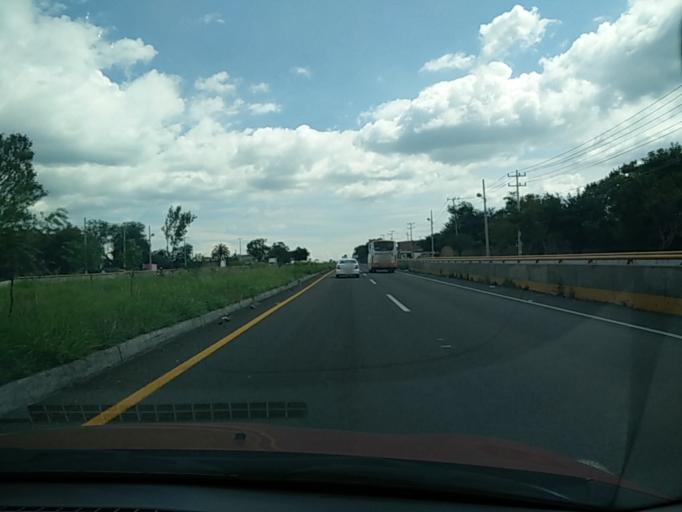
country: MX
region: Jalisco
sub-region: Ixtlahuacan de los Membrillos
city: Los Olivos
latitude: 20.4508
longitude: -103.2488
